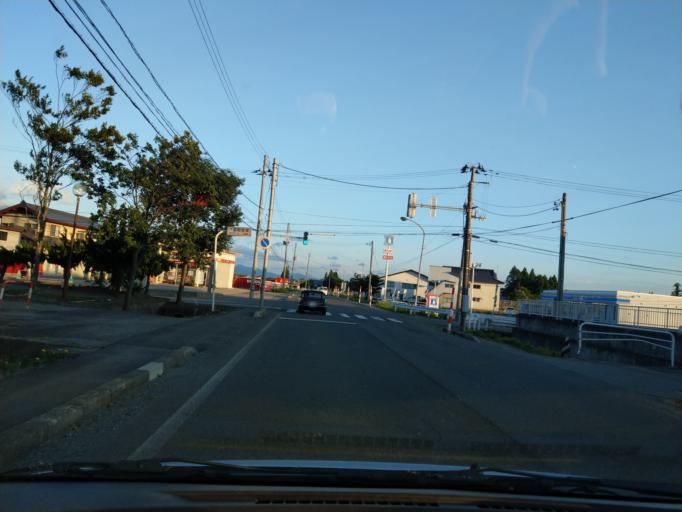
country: JP
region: Akita
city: Kakunodatemachi
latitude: 39.6558
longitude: 140.5707
